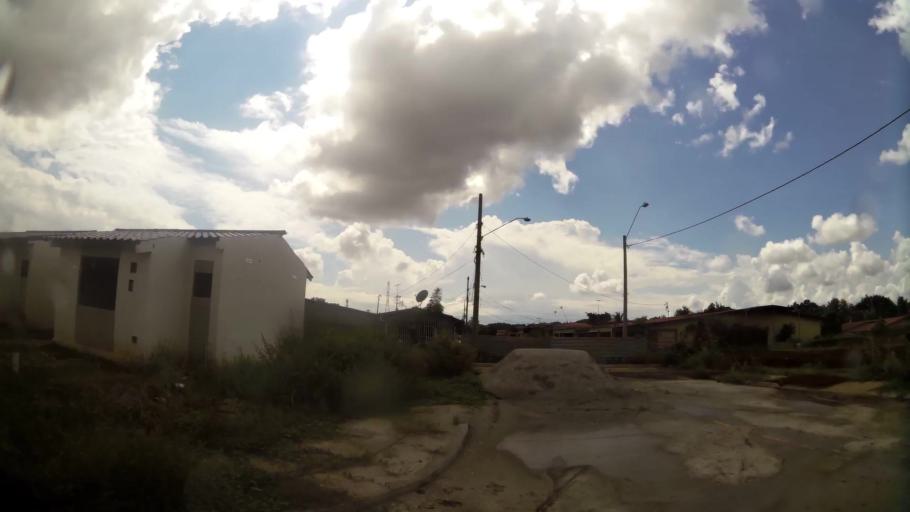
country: PA
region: Panama
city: Nuevo Arraijan
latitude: 8.9362
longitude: -79.7369
